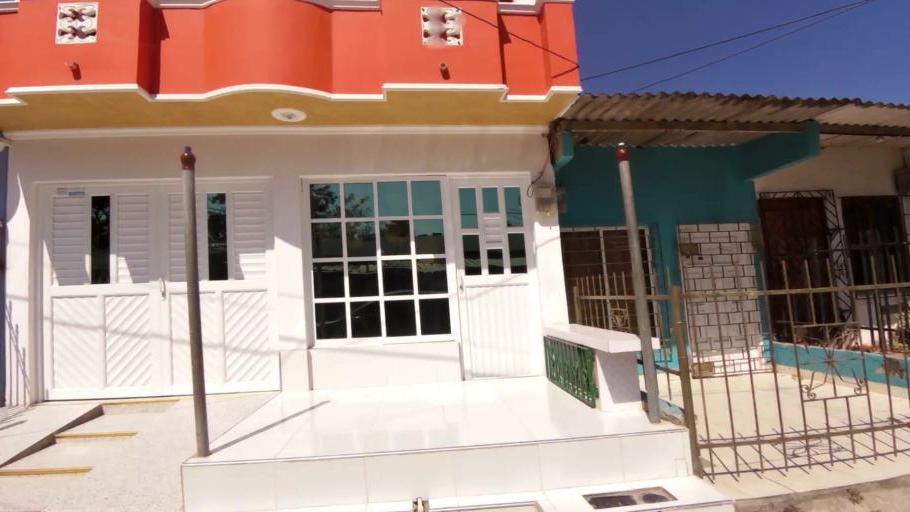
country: CO
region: Bolivar
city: Cartagena
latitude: 10.3560
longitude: -75.4911
